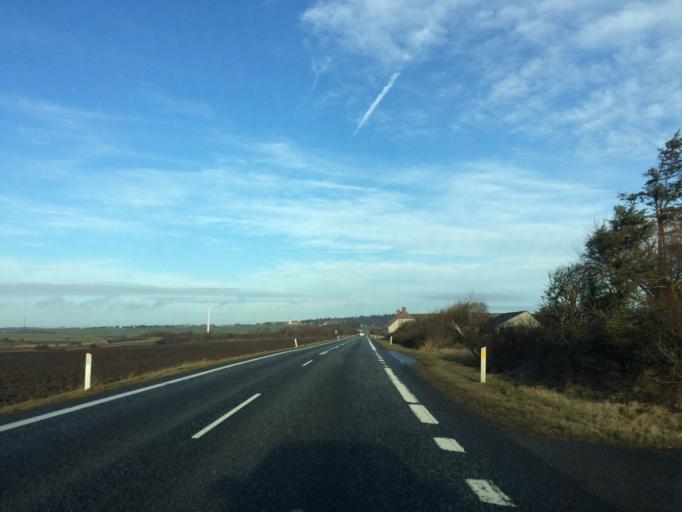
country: DK
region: North Denmark
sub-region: Thisted Kommune
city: Hurup
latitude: 56.6947
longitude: 8.4035
